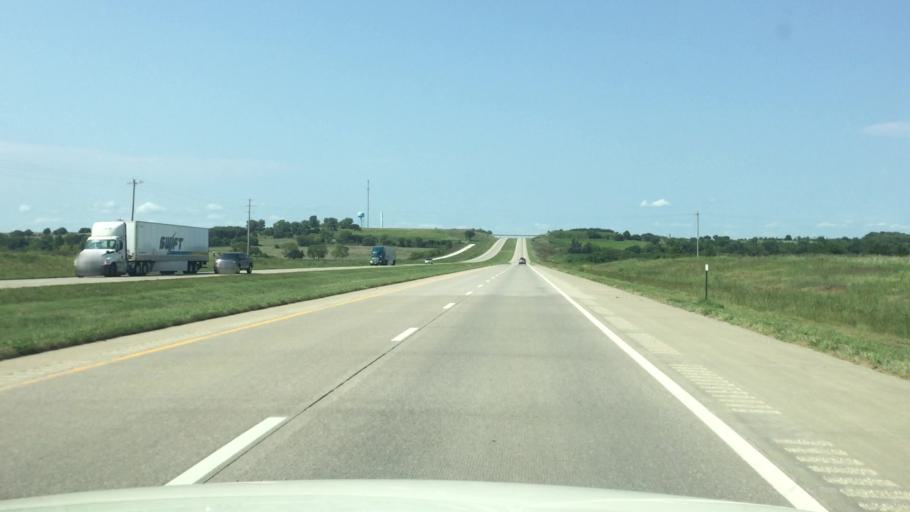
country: US
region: Kansas
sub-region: Linn County
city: Pleasanton
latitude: 38.0934
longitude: -94.7133
